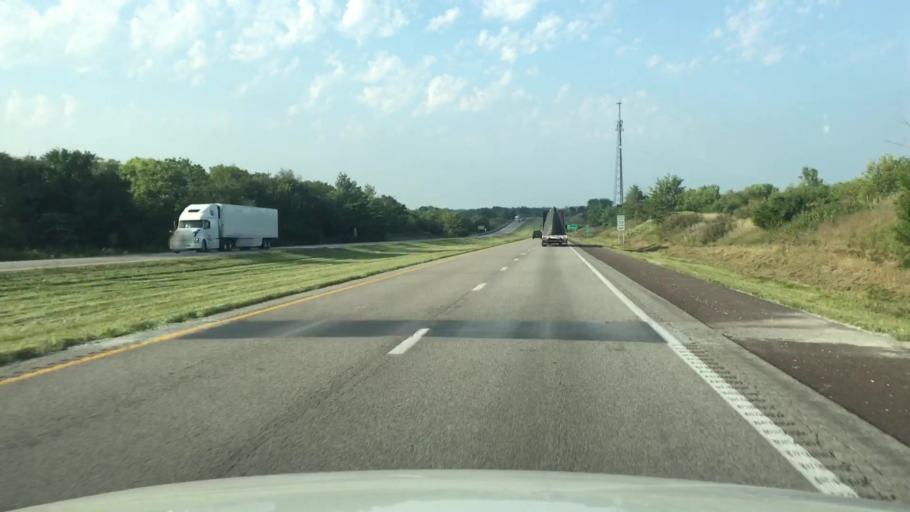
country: US
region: Missouri
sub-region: Clinton County
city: Cameron
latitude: 39.8620
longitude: -94.1729
